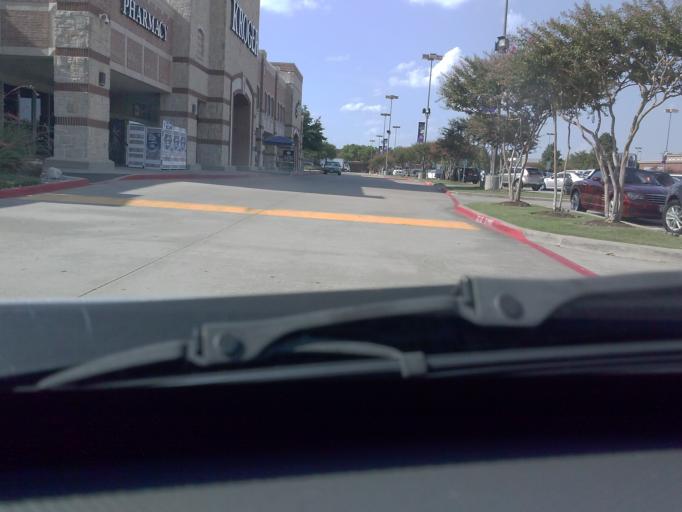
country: US
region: Texas
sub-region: Denton County
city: The Colony
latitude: 33.0471
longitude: -96.8315
